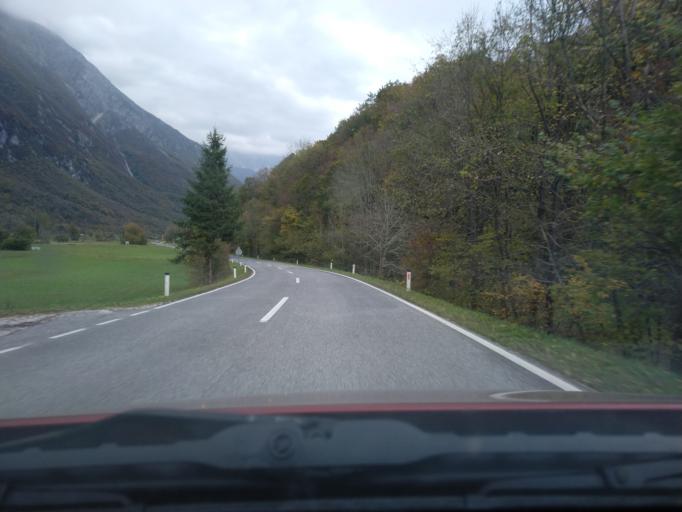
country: SI
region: Kobarid
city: Kobarid
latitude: 46.2811
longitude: 13.5412
